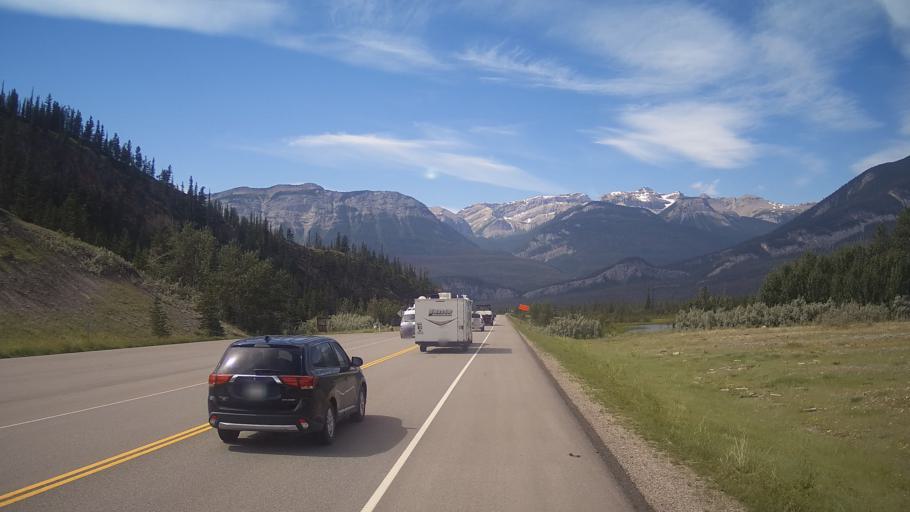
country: CA
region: Alberta
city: Jasper Park Lodge
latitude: 53.0448
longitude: -118.0829
